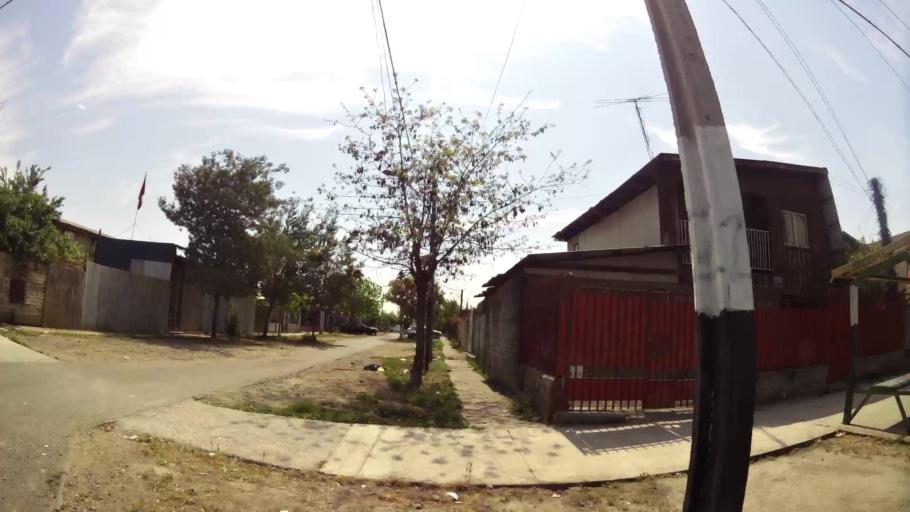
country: CL
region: Santiago Metropolitan
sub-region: Provincia de Santiago
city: La Pintana
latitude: -33.5551
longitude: -70.6539
